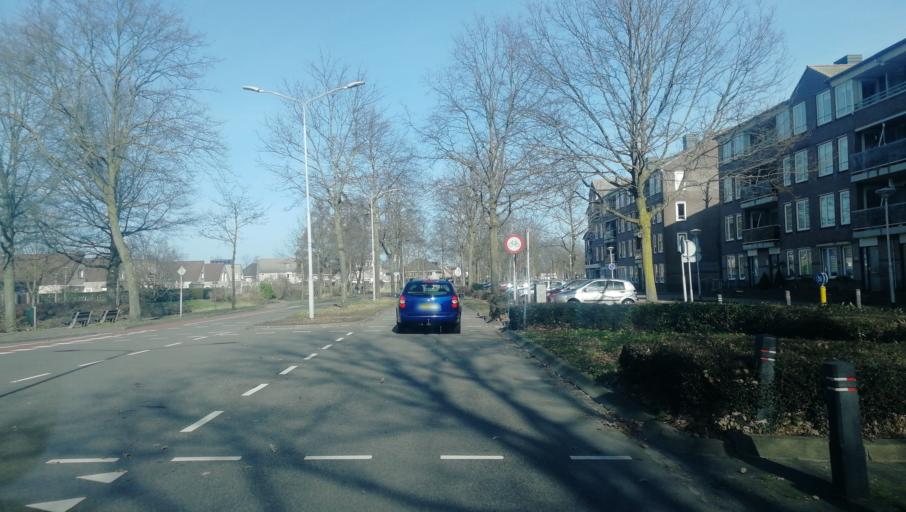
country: NL
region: Limburg
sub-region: Gemeente Venlo
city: Venlo
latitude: 51.3631
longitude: 6.1816
